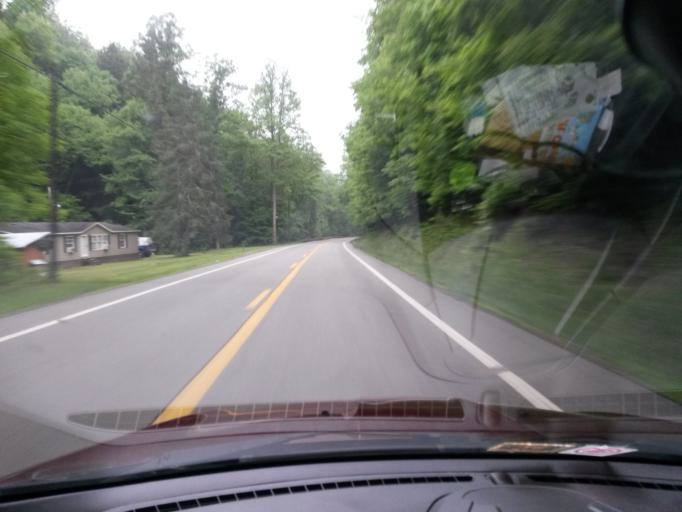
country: US
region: West Virginia
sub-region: Wyoming County
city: Pineville
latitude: 37.5398
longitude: -81.5878
